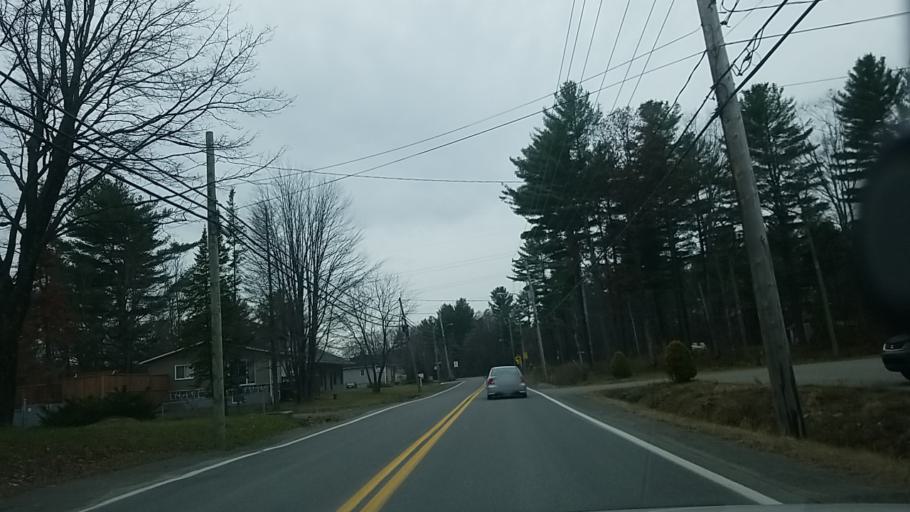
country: CA
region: Quebec
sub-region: Laurentides
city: Saint-Jerome
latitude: 45.7891
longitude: -74.0648
